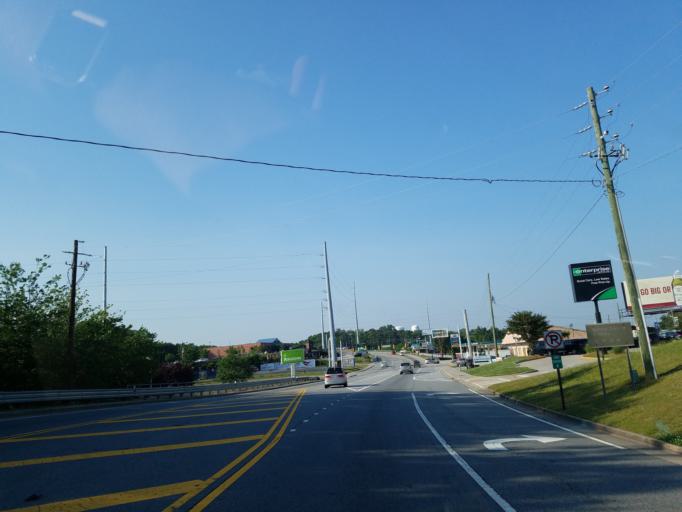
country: US
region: Georgia
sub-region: Forsyth County
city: Cumming
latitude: 34.1964
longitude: -84.1357
